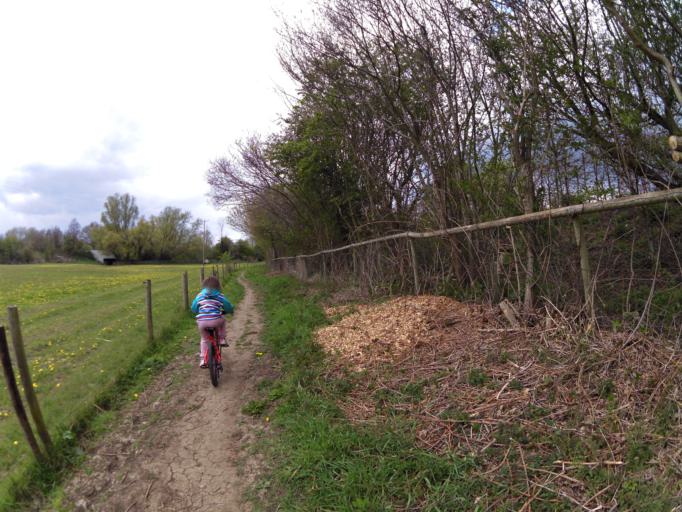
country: GB
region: England
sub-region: Suffolk
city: Bramford
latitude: 52.0365
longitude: 1.0925
